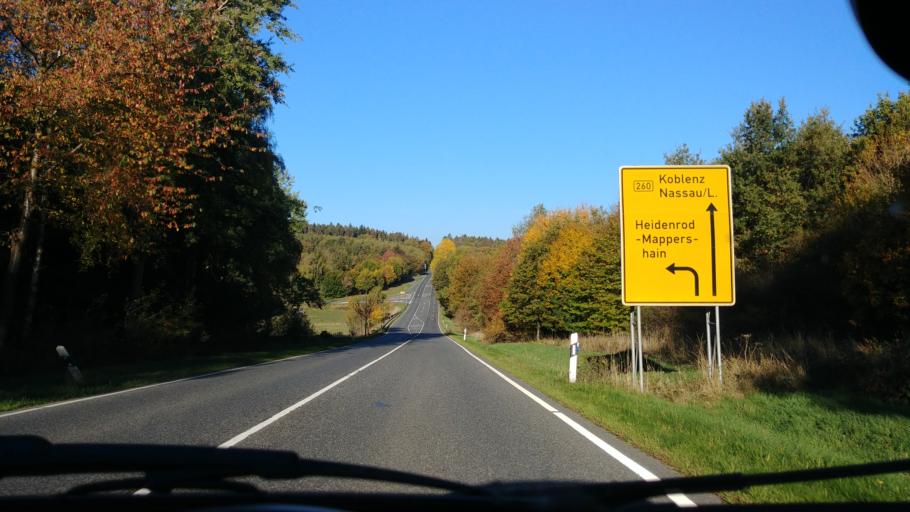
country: DE
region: Rheinland-Pfalz
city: Reckenroth
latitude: 50.1717
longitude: 8.0078
